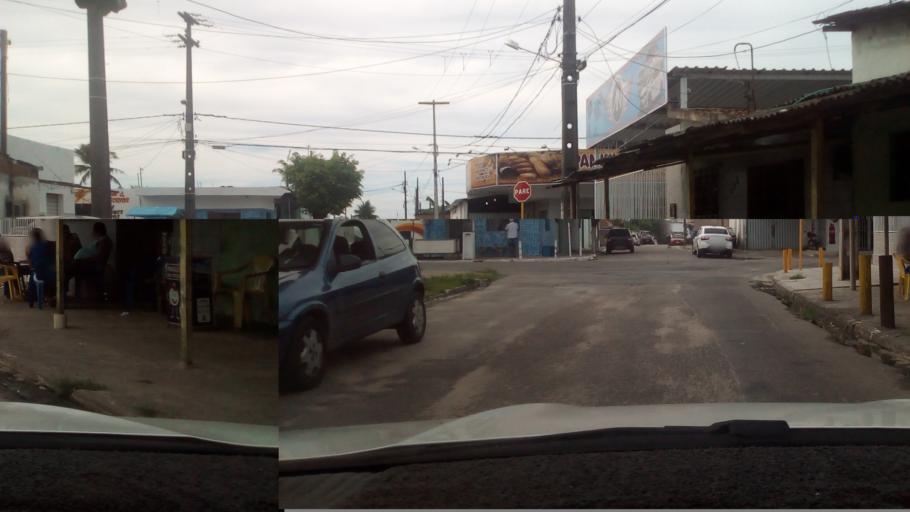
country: BR
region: Paraiba
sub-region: Joao Pessoa
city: Joao Pessoa
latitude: -7.1464
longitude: -34.8726
